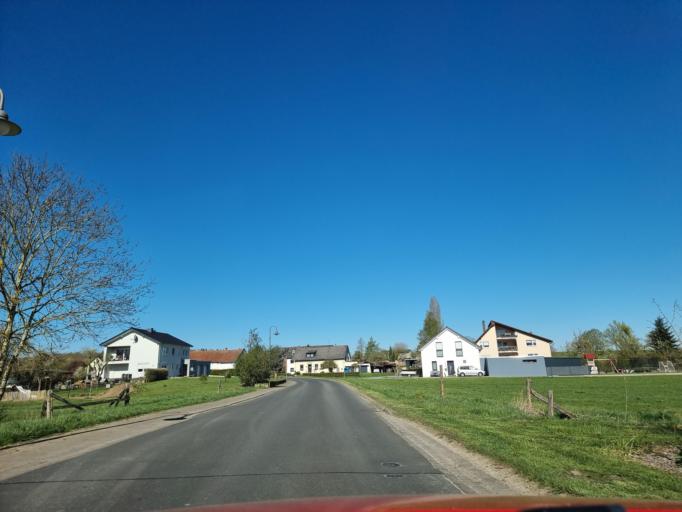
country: DE
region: Rheinland-Pfalz
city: Idenheim
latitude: 49.8986
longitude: 6.5668
